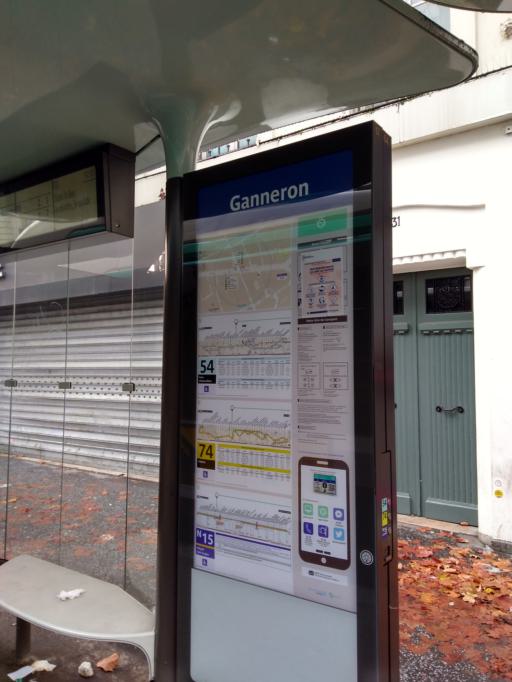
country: FR
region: Ile-de-France
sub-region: Paris
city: Saint-Ouen
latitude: 48.8861
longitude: 2.3262
